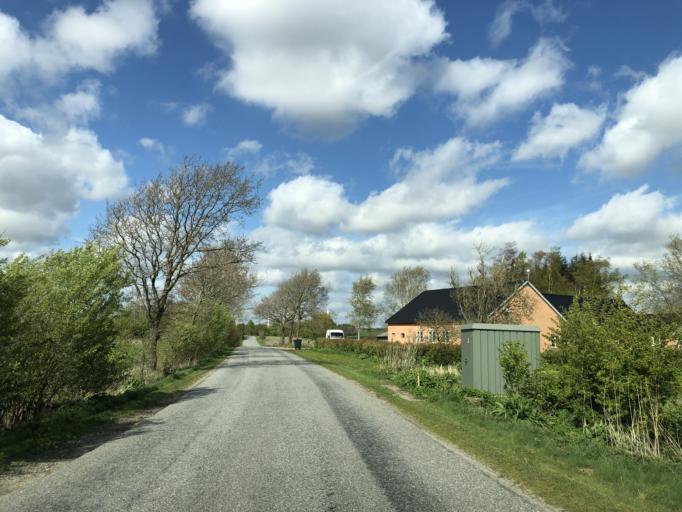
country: DK
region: Central Jutland
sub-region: Herning Kommune
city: Avlum
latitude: 56.2697
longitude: 8.6912
